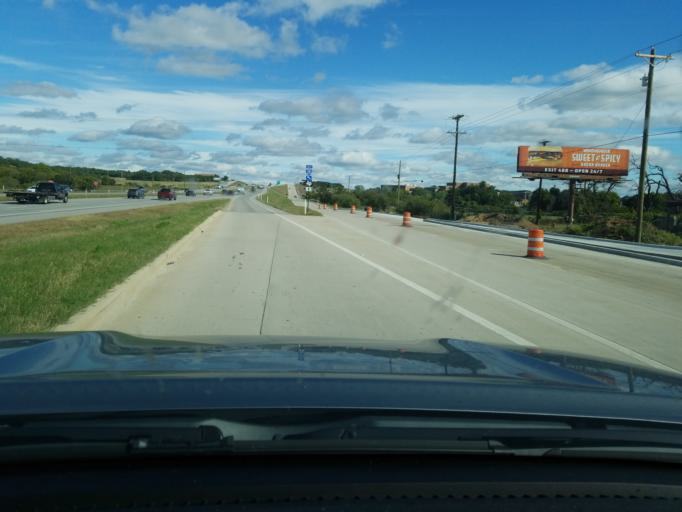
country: US
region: Texas
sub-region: Parker County
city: Weatherford
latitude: 32.7275
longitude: -97.8133
